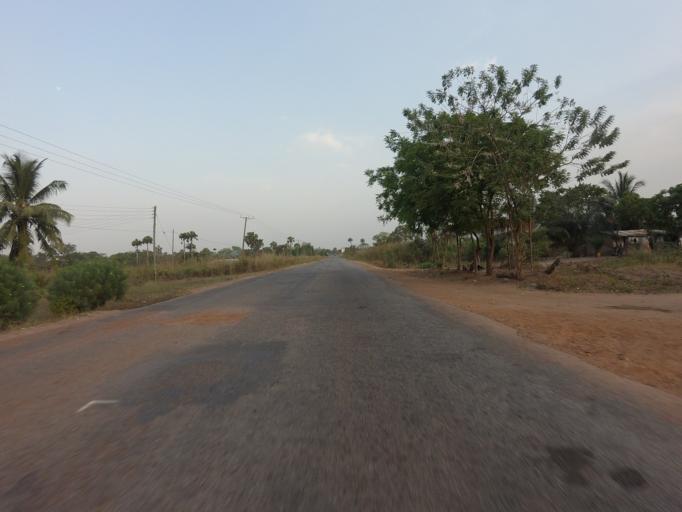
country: GH
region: Volta
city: Ho
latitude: 6.5723
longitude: 0.3865
